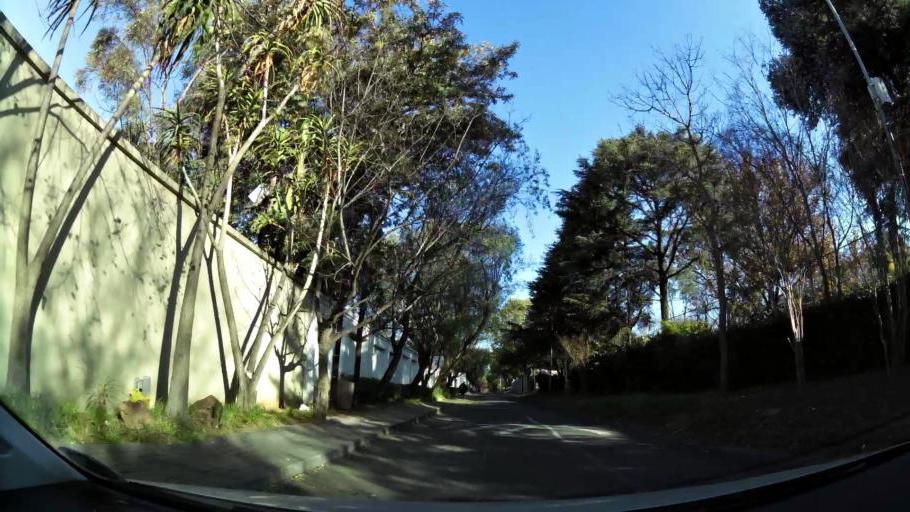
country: ZA
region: Gauteng
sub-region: City of Johannesburg Metropolitan Municipality
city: Johannesburg
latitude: -26.1091
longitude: 28.0662
